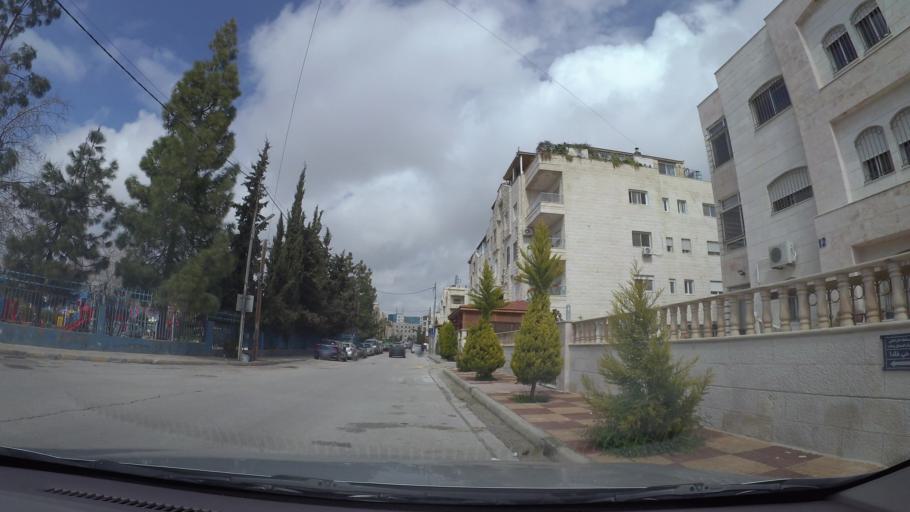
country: JO
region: Amman
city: Al Jubayhah
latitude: 31.9927
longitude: 35.8473
